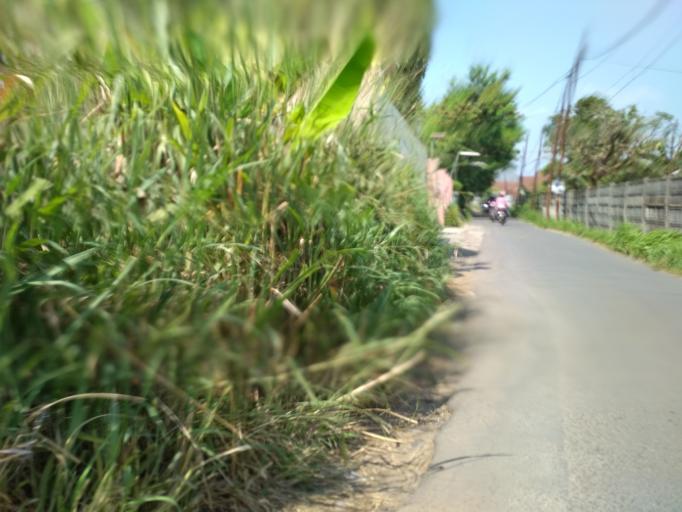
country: ID
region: West Java
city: Ciampea
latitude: -6.5618
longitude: 106.7436
